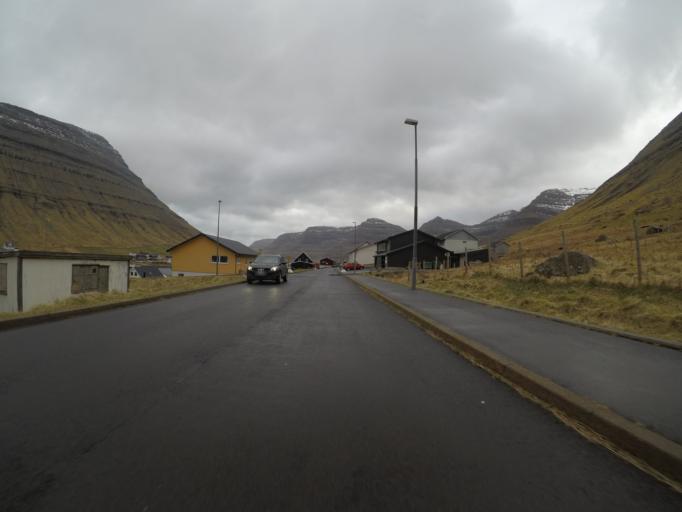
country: FO
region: Nordoyar
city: Klaksvik
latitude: 62.2992
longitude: -6.5301
